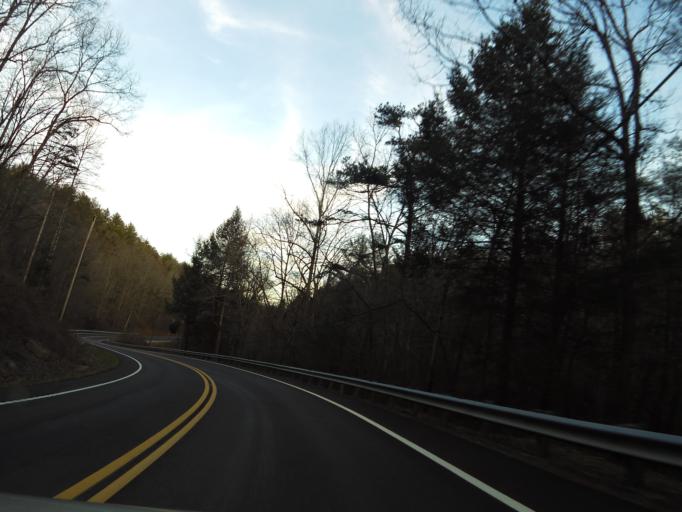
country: US
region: Tennessee
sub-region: Roane County
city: Rockwood
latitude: 35.8722
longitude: -84.7810
